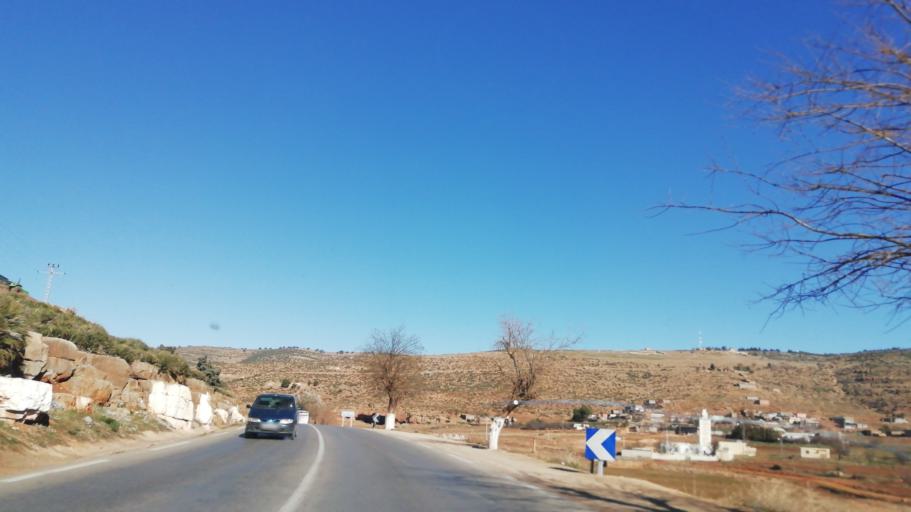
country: DZ
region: Tlemcen
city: Sebdou
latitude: 34.6946
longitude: -1.3125
